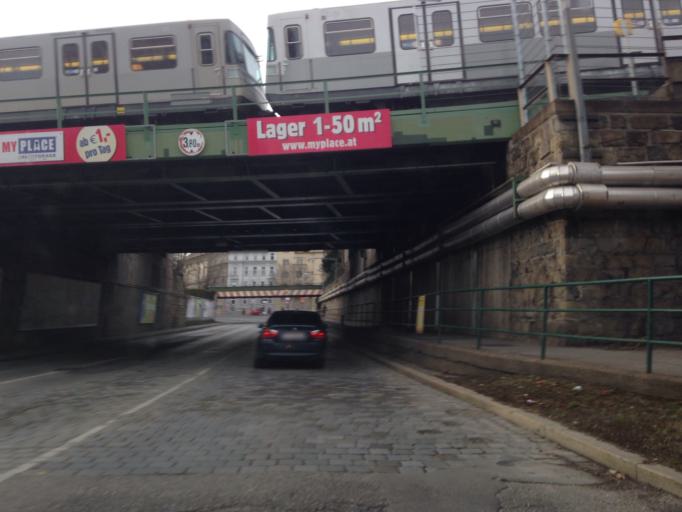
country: AT
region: Vienna
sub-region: Wien Stadt
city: Vienna
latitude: 48.2453
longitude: 16.3647
